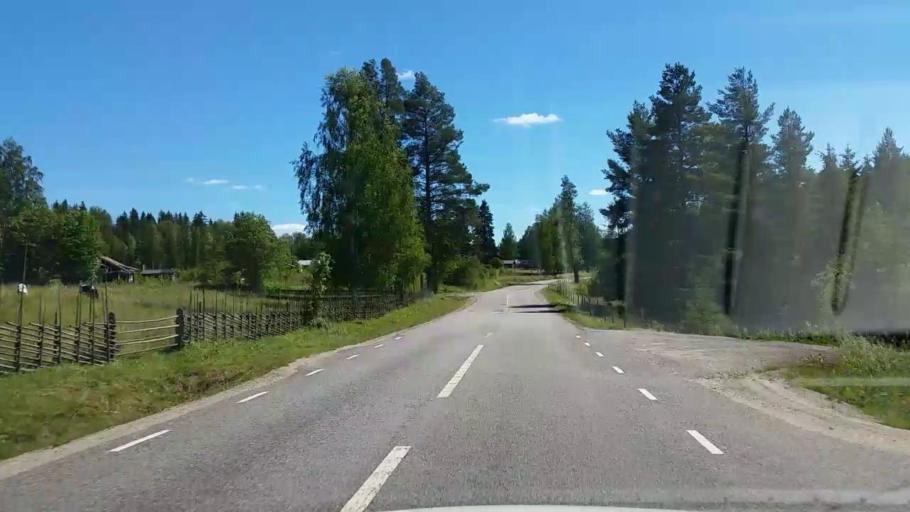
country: SE
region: Gaevleborg
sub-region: Ovanakers Kommun
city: Edsbyn
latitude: 61.4546
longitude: 15.7059
